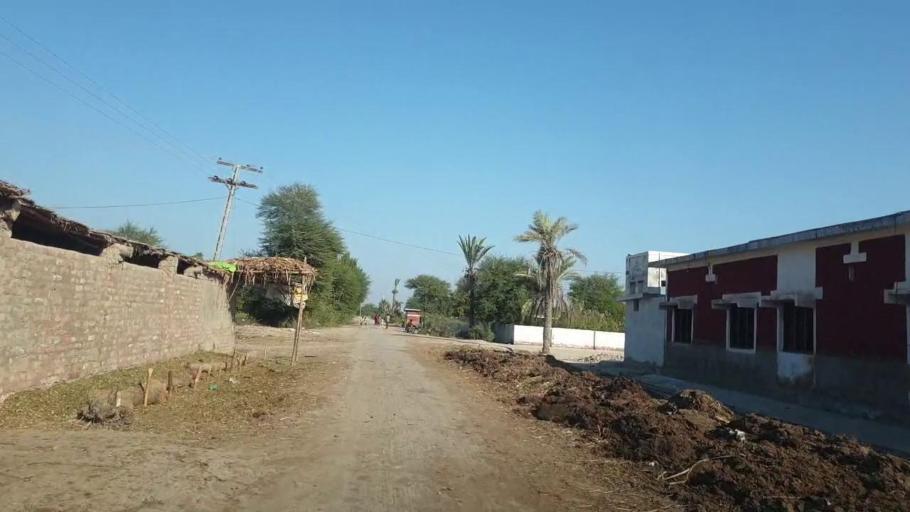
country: PK
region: Sindh
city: Mirpur Khas
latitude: 25.6191
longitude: 69.0782
